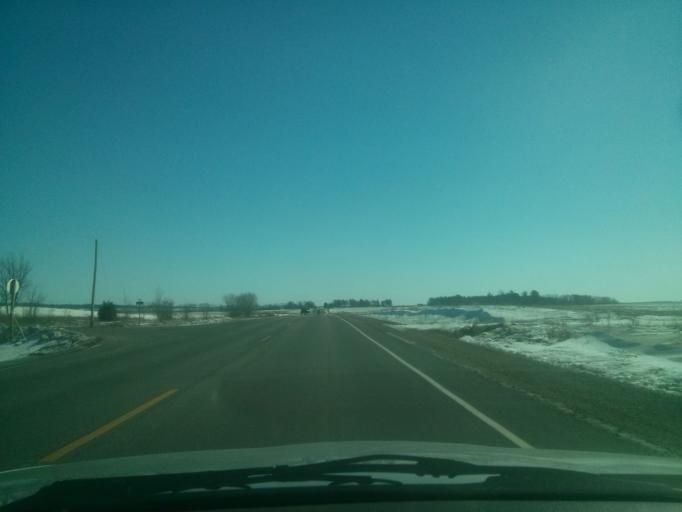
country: US
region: Wisconsin
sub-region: Polk County
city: Clear Lake
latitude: 45.1364
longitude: -92.3637
